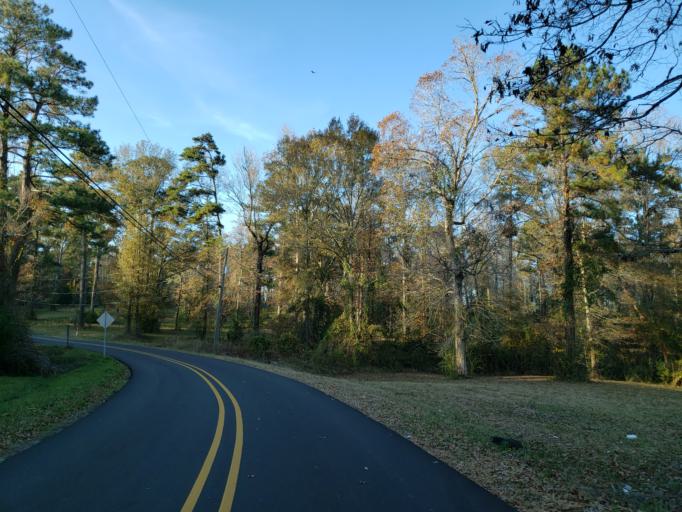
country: US
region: Mississippi
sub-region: Lamar County
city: Arnold Line
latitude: 31.3497
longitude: -89.3534
